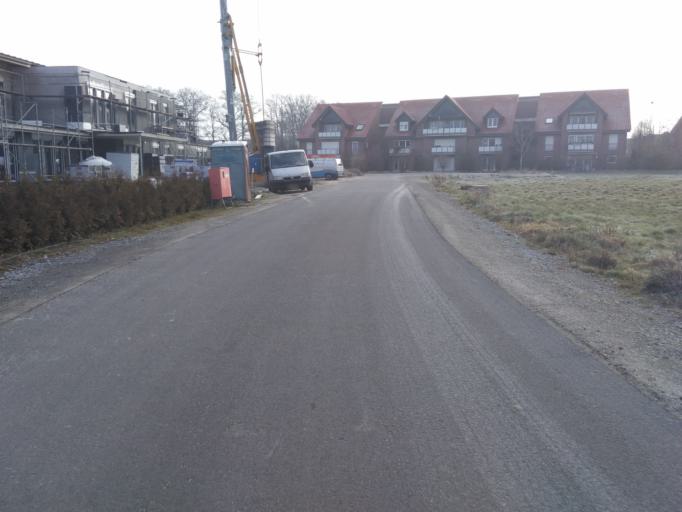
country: DE
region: North Rhine-Westphalia
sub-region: Regierungsbezirk Detmold
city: Verl
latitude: 51.8847
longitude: 8.4972
